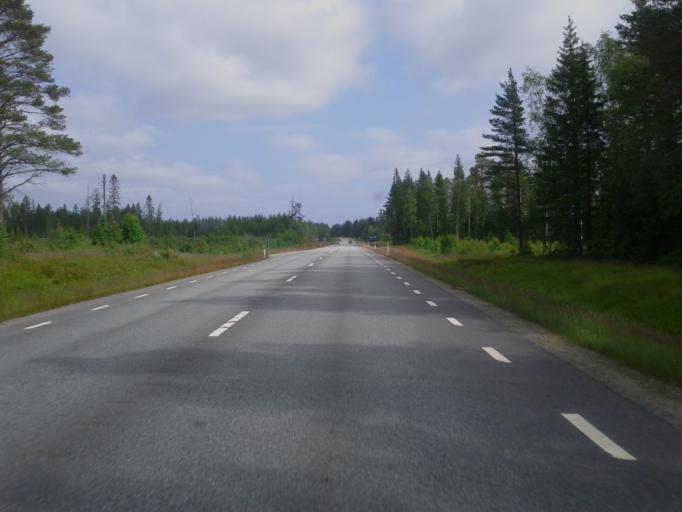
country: SE
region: Vaesterbotten
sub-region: Skelleftea Kommun
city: Burea
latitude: 64.3436
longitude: 21.2834
